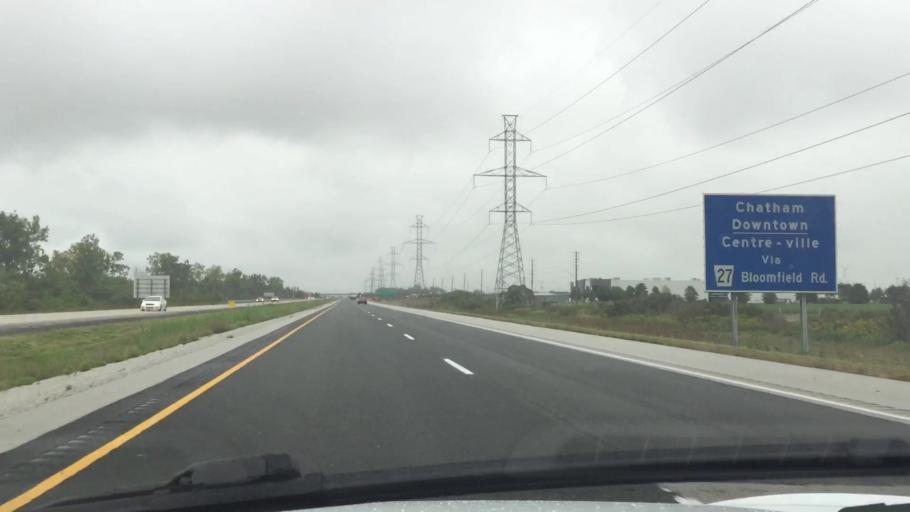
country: CA
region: Ontario
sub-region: Lambton County
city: Walpole Island
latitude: 42.3424
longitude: -82.1966
